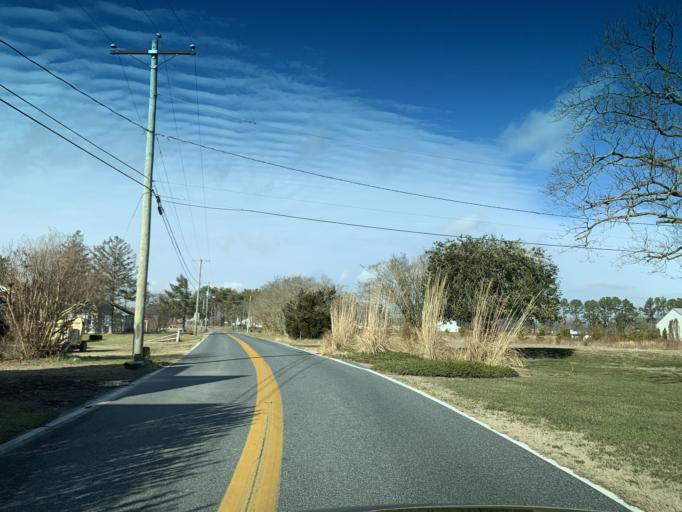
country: US
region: Delaware
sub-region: Sussex County
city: Selbyville
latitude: 38.4502
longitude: -75.1944
